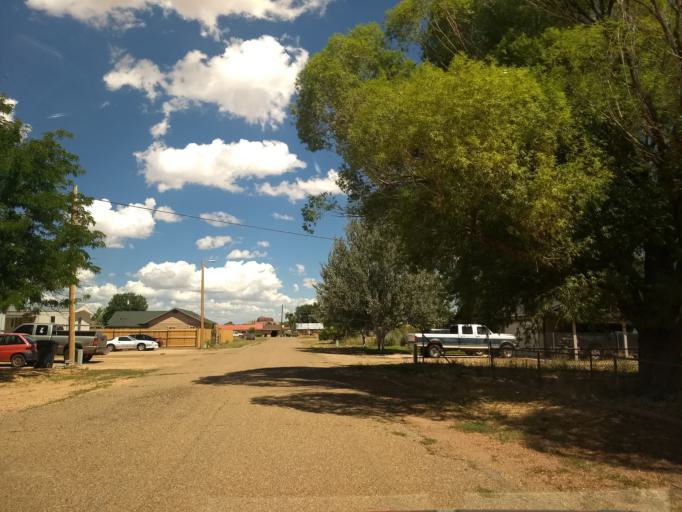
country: US
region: Arizona
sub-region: Coconino County
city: Fredonia
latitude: 36.9496
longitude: -112.5230
